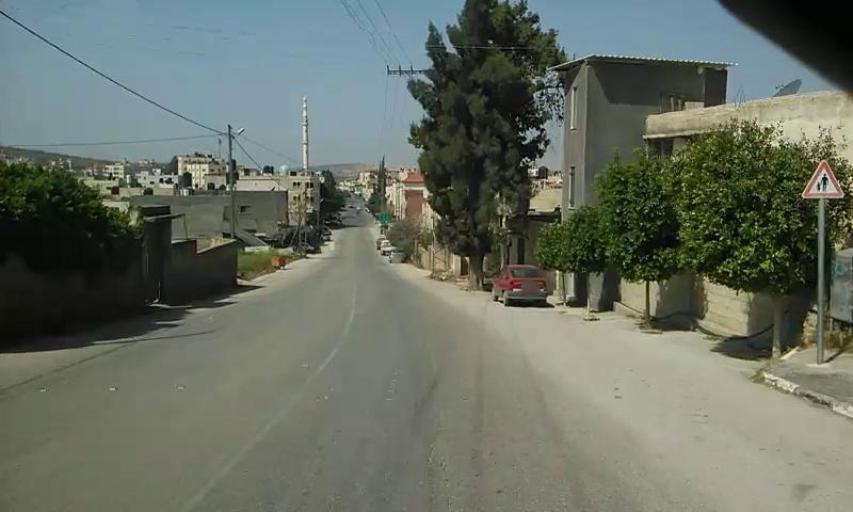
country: PS
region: West Bank
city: Az Zababidah
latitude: 32.3839
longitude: 35.3262
